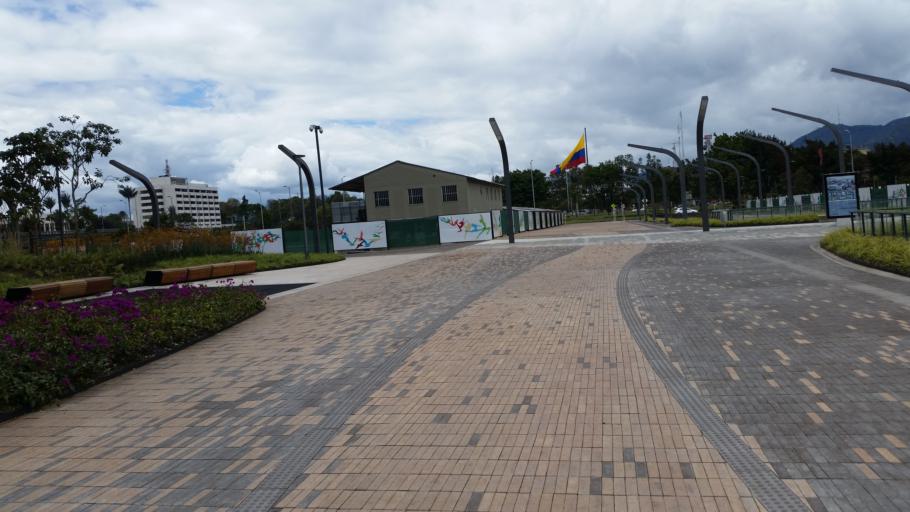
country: CO
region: Bogota D.C.
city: Bogota
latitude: 4.6436
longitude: -74.0992
